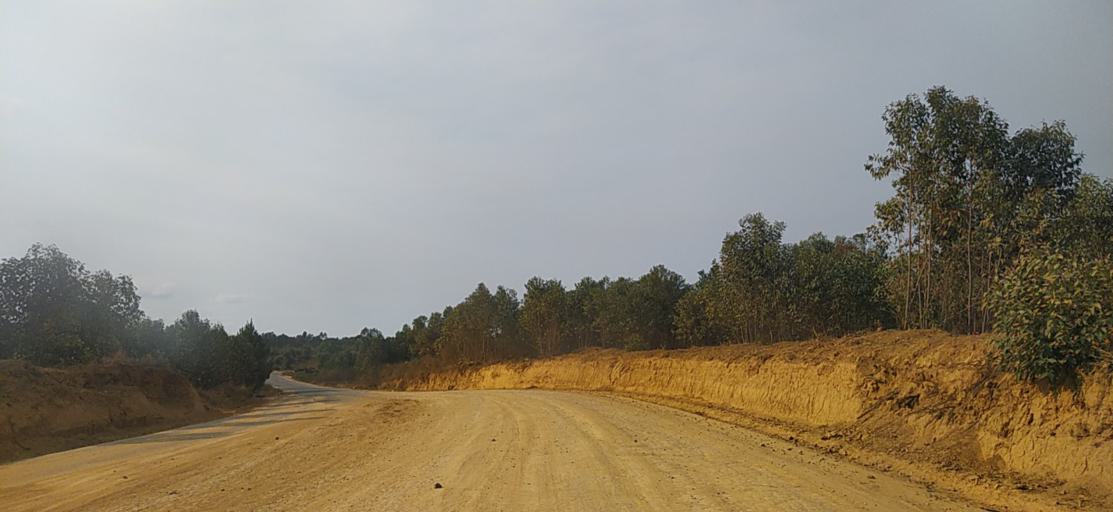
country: MG
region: Alaotra Mangoro
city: Moramanga
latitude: -18.6544
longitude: 48.2746
